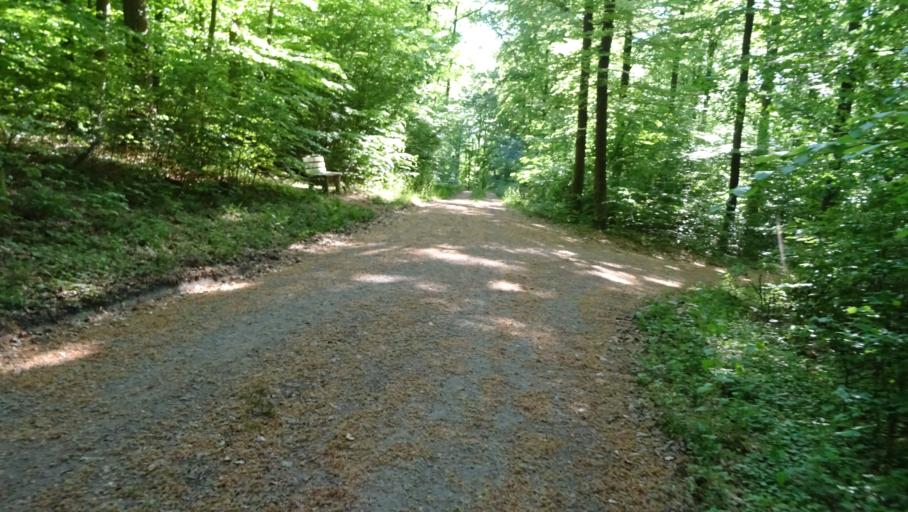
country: DE
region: Baden-Wuerttemberg
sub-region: Karlsruhe Region
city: Neckarzimmern
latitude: 49.3263
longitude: 9.1259
